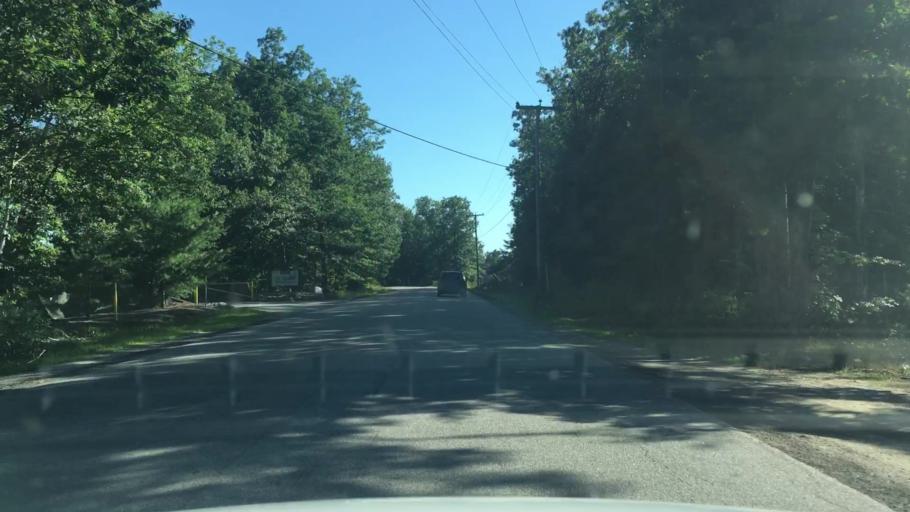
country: US
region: New Hampshire
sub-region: Rockingham County
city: Brentwood
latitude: 43.0066
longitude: -71.0125
